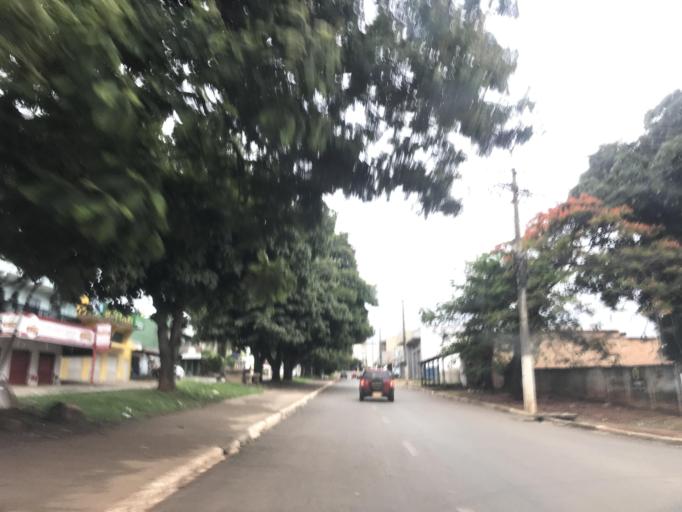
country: BR
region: Goias
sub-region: Luziania
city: Luziania
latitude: -16.2614
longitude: -47.9577
